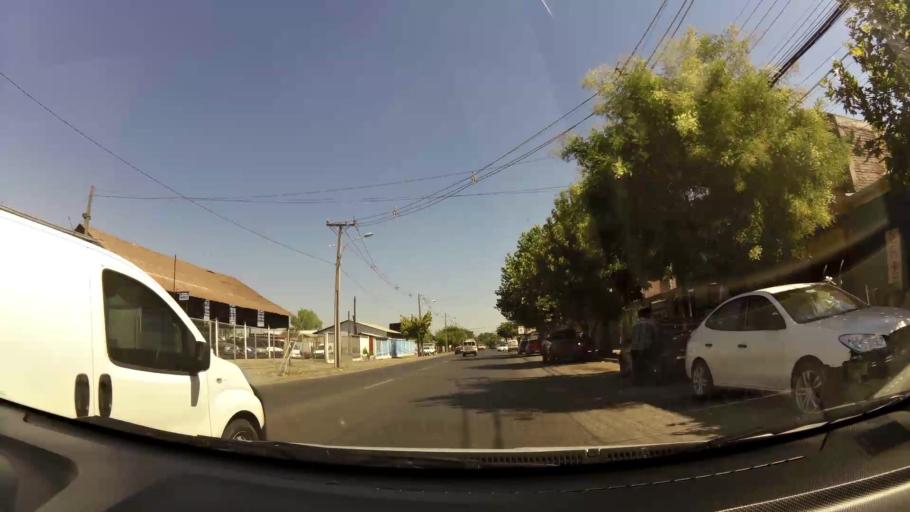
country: CL
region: Maule
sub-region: Provincia de Talca
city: Talca
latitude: -35.4336
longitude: -71.6510
